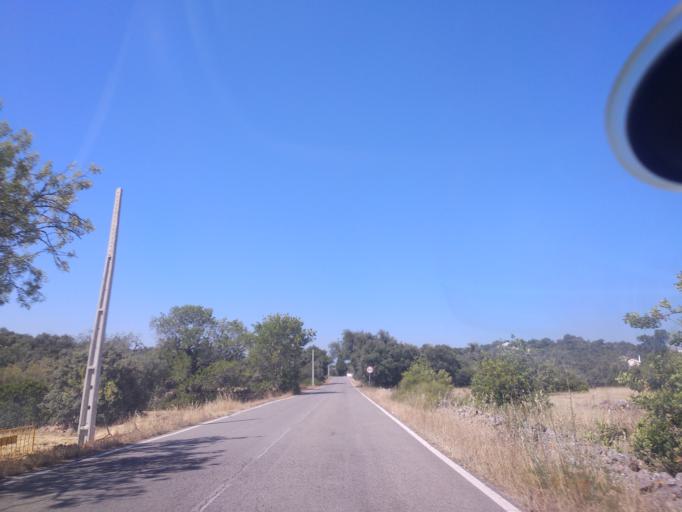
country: PT
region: Faro
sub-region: Sao Bras de Alportel
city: Sao Bras de Alportel
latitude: 37.1609
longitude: -7.9328
